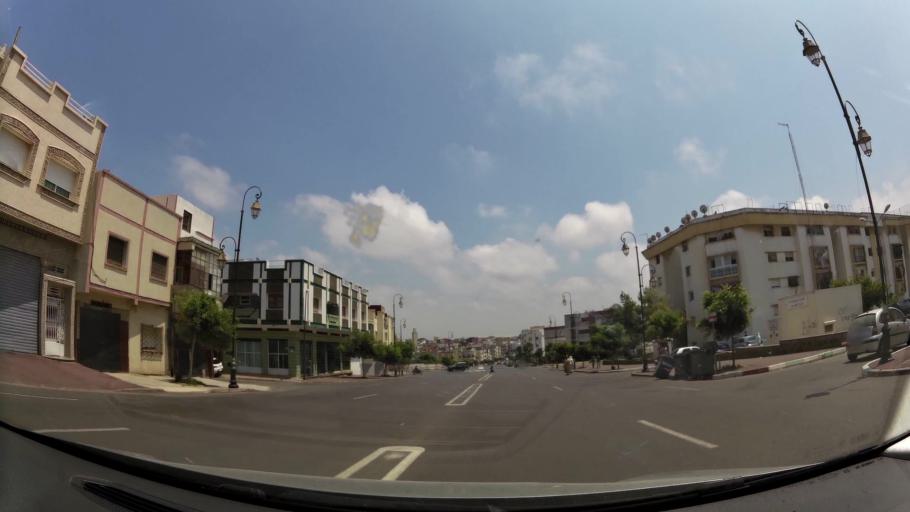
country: MA
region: Rabat-Sale-Zemmour-Zaer
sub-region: Skhirate-Temara
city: Temara
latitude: 33.9726
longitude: -6.8969
